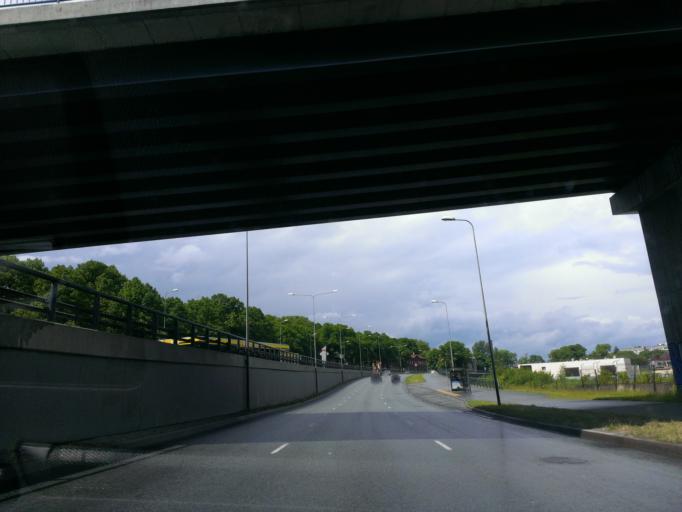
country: LV
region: Riga
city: Riga
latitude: 56.9502
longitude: 24.0747
